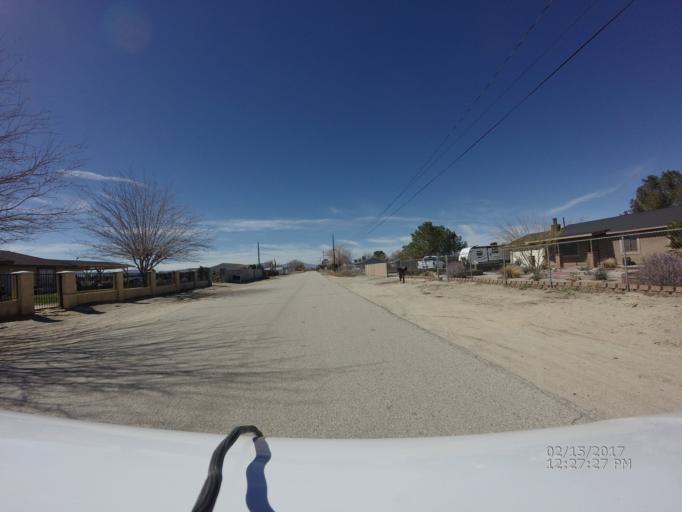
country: US
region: California
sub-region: Los Angeles County
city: Littlerock
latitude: 34.5817
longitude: -117.9544
